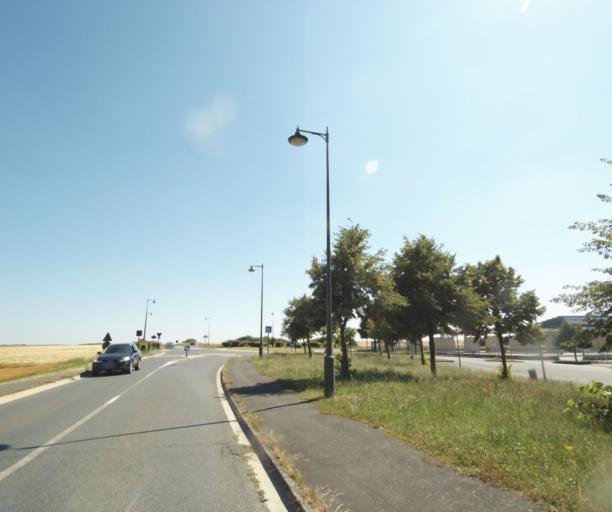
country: FR
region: Ile-de-France
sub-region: Departement de Seine-et-Marne
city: La Chapelle-la-Reine
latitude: 48.3094
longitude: 2.5728
